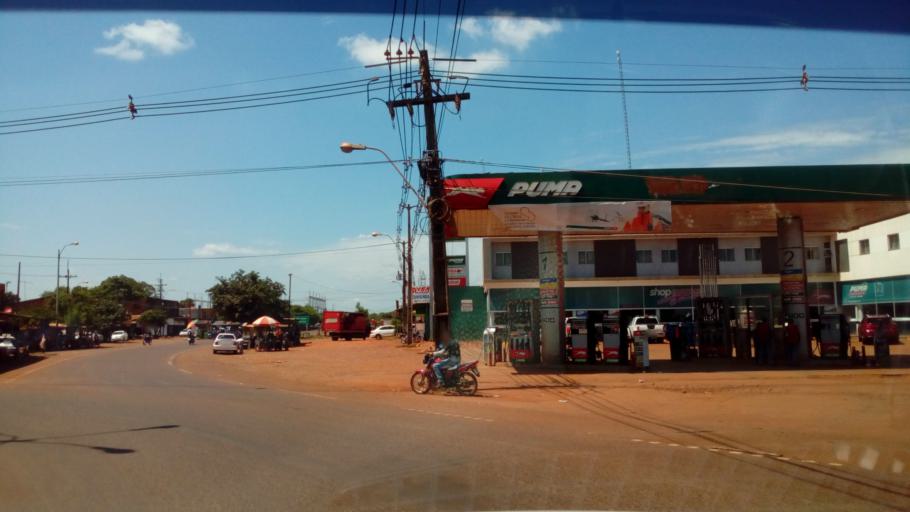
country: PY
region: Alto Parana
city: Colonia Yguazu
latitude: -25.4838
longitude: -54.8976
